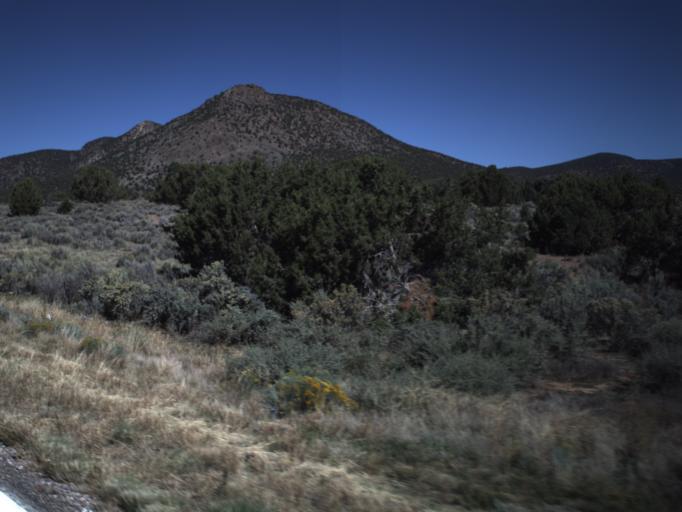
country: US
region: Utah
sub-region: Washington County
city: Enterprise
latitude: 37.6489
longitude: -113.4476
